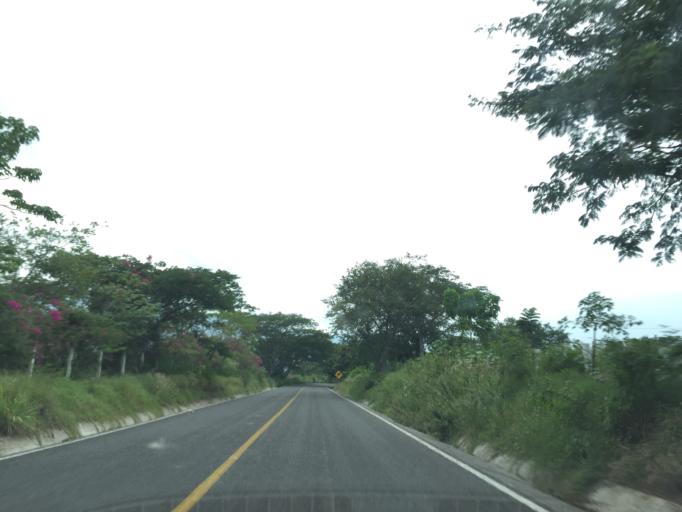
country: MX
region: Colima
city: Comala
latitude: 19.3550
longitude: -103.7933
